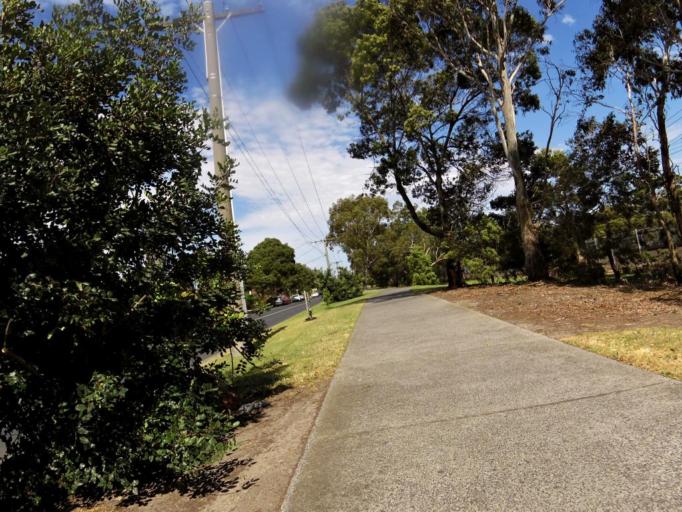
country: AU
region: Victoria
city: Clayton
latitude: -37.9213
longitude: 145.1164
